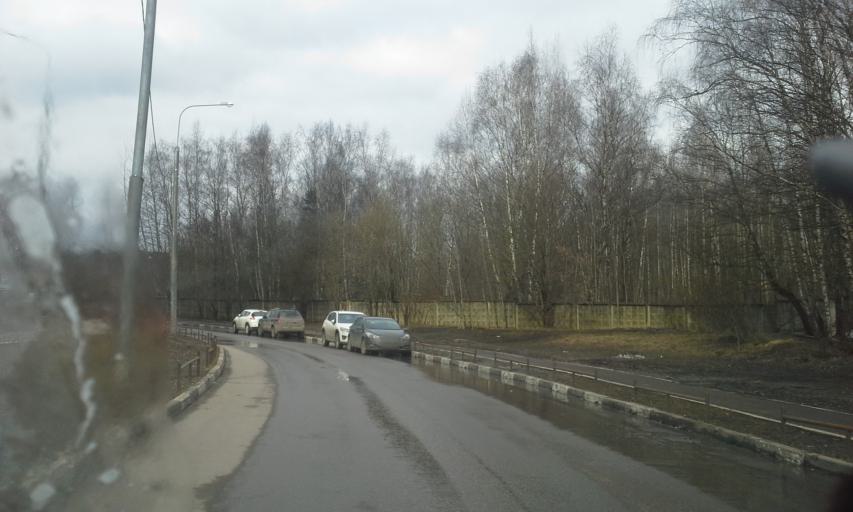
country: RU
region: Moskovskaya
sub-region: Leninskiy Rayon
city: Vnukovo
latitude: 55.6238
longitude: 37.3153
